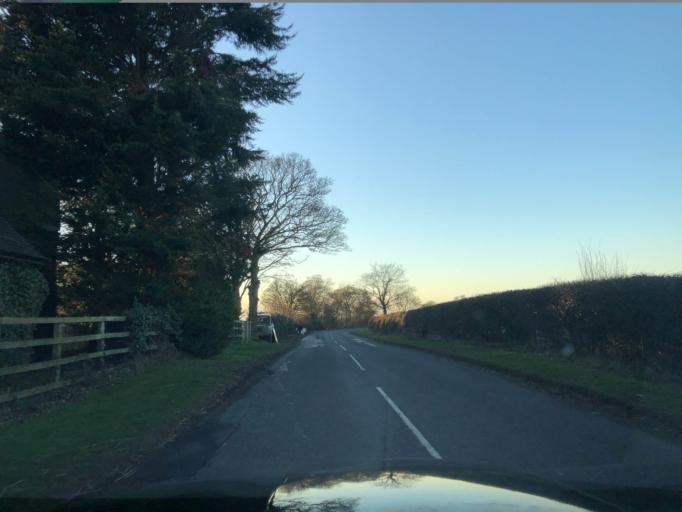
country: GB
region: England
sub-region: Warwickshire
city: Harbury
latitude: 52.2268
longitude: -1.4629
